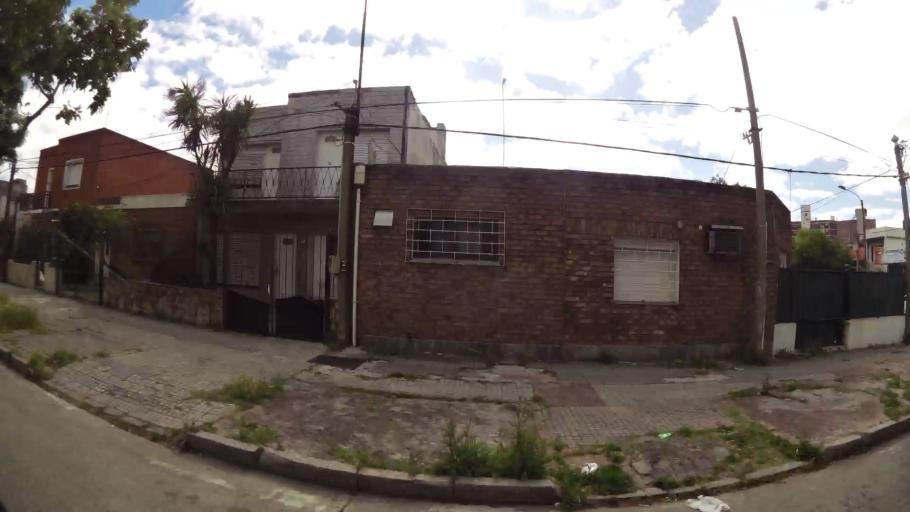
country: UY
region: Montevideo
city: Montevideo
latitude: -34.8931
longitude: -56.1314
